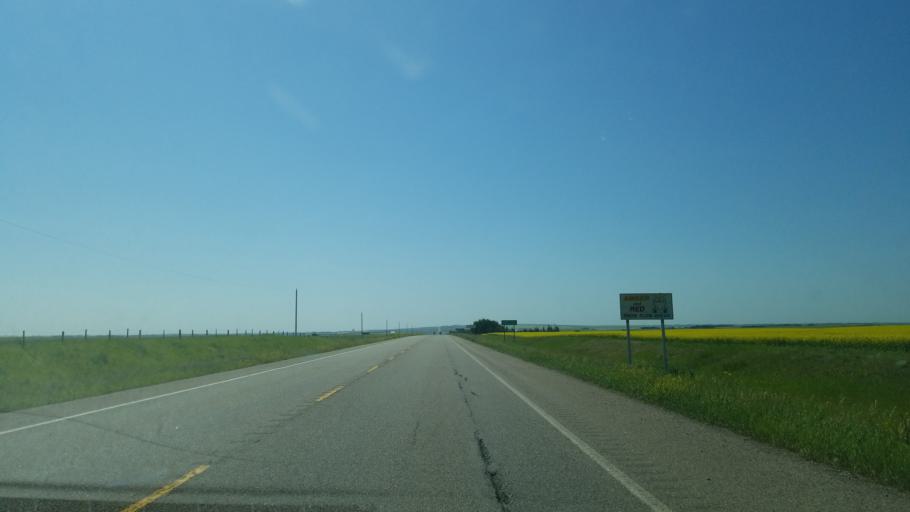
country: CA
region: Saskatchewan
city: Macklin
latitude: 52.3613
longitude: -110.0212
